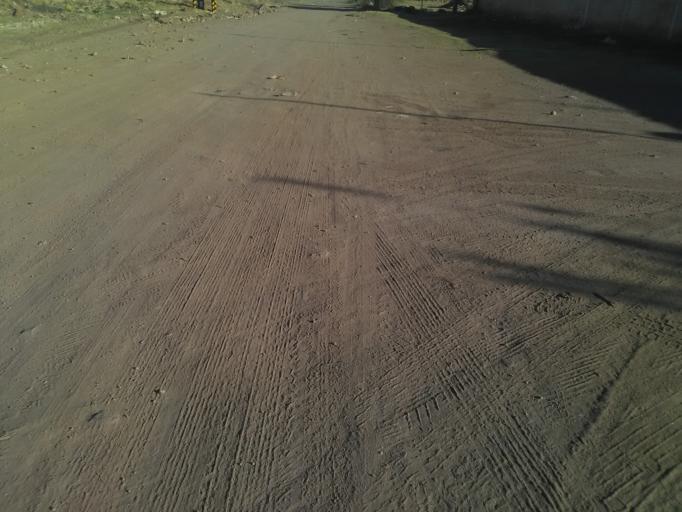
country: MX
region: Durango
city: Victoria de Durango
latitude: 24.0573
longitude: -104.6543
